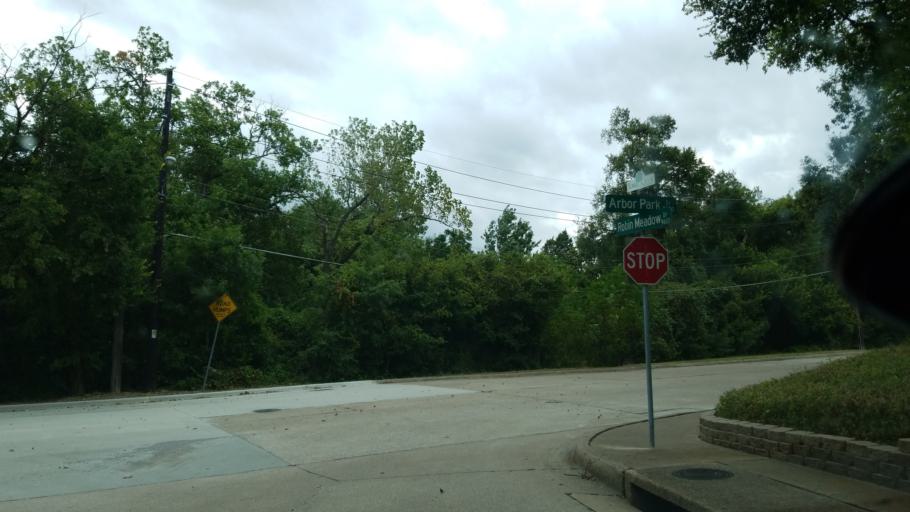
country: US
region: Texas
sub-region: Dallas County
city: Richardson
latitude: 32.8986
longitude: -96.7295
